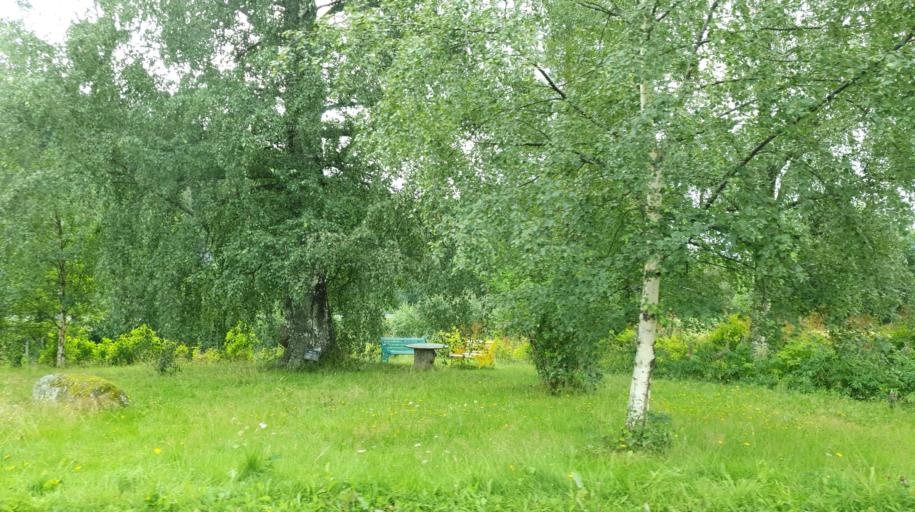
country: NO
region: Nord-Trondelag
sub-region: Stjordal
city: Stjordalshalsen
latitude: 63.4490
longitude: 10.9912
